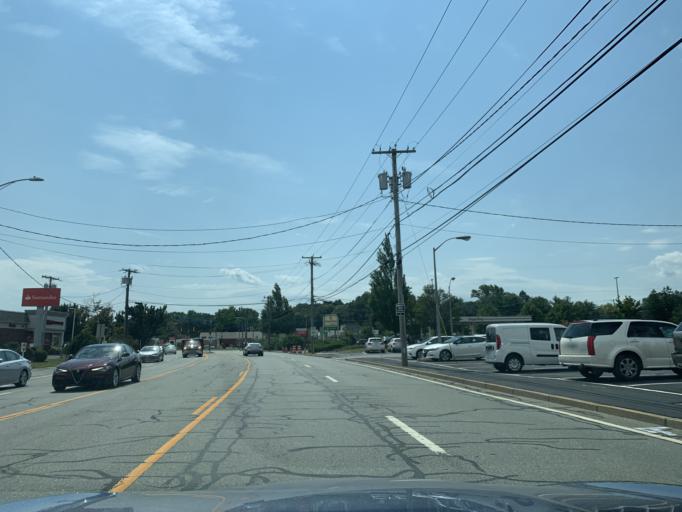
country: US
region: Rhode Island
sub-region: Providence County
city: Cranston
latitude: 41.7825
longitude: -71.4730
